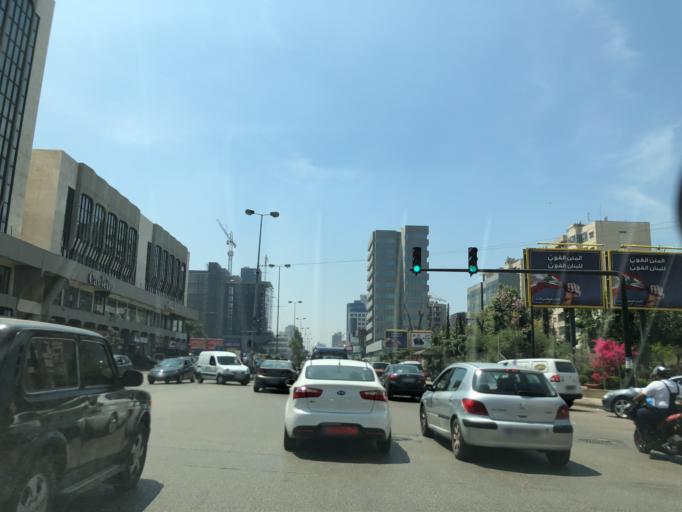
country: LB
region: Mont-Liban
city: Jdaidet el Matn
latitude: 33.8896
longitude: 35.5542
